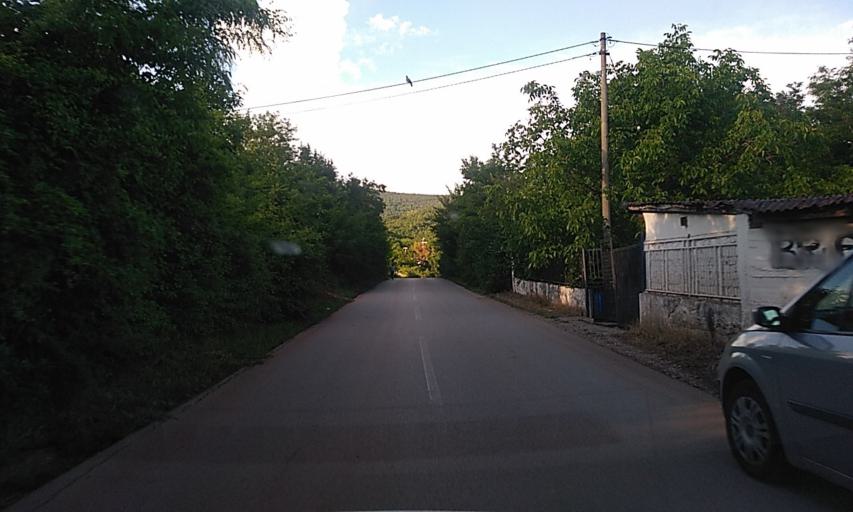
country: RS
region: Central Serbia
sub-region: Nisavski Okrug
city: Niska Banja
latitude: 43.3675
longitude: 21.9831
